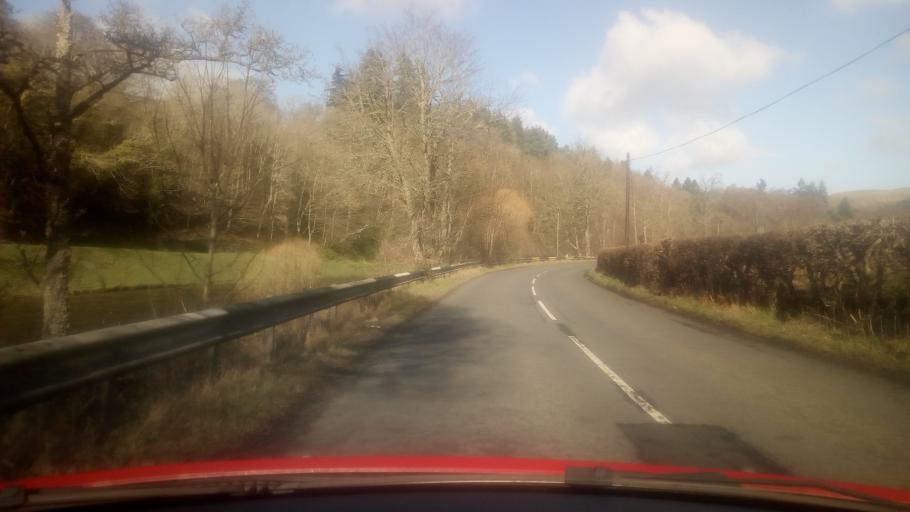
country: GB
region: Scotland
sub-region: The Scottish Borders
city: Selkirk
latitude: 55.5881
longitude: -2.8686
